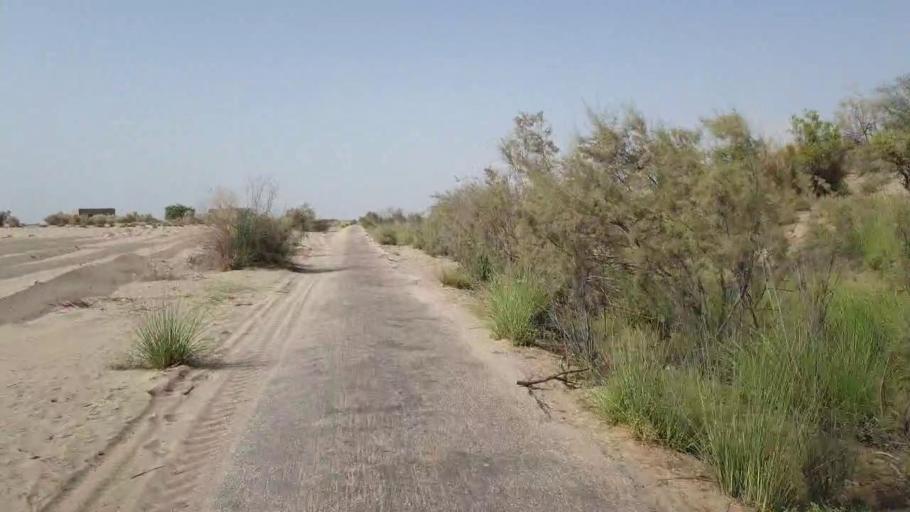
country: PK
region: Sindh
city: Jam Sahib
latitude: 26.5986
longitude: 68.9241
